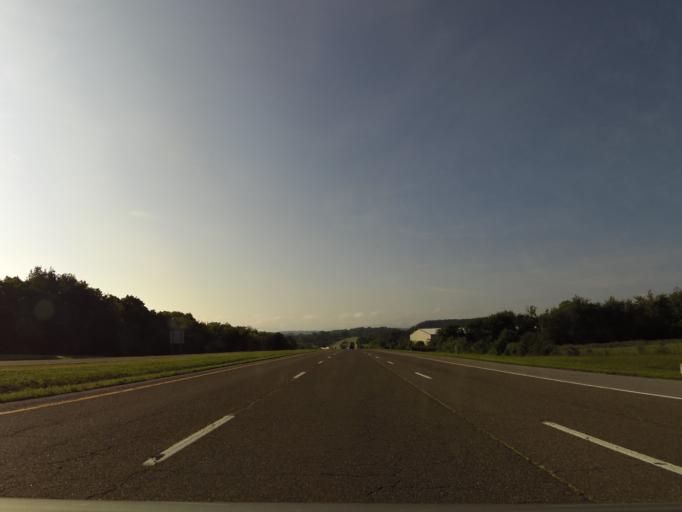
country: US
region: Tennessee
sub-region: Blount County
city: Alcoa
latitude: 35.8326
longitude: -83.9658
